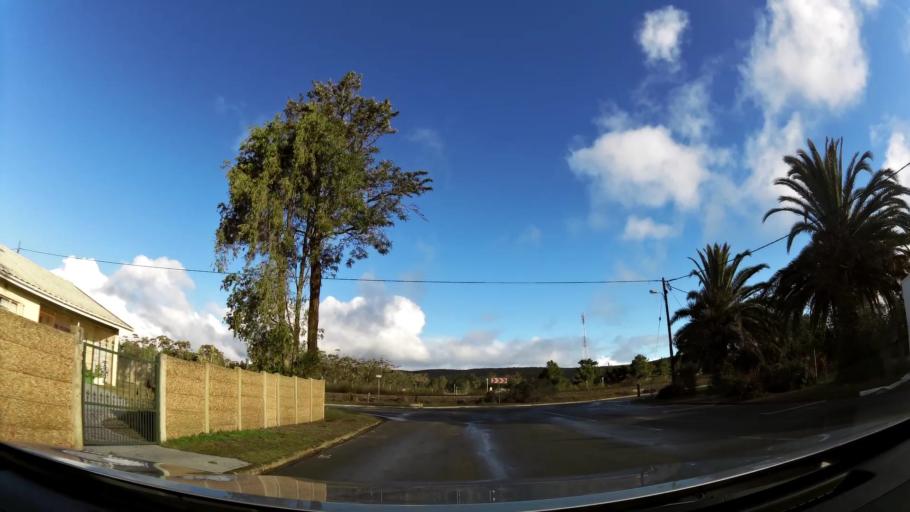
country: ZA
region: Western Cape
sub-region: Eden District Municipality
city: Riversdale
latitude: -34.2087
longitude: 21.5865
